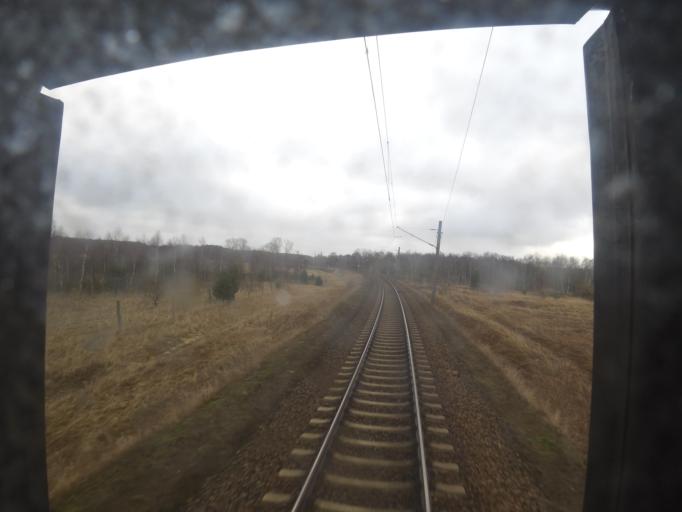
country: DE
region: Brandenburg
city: Ludwigsfelde
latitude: 52.3320
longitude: 13.2612
